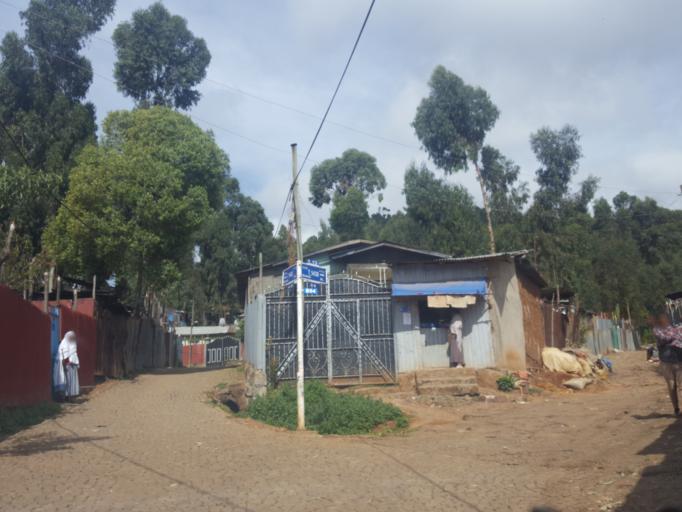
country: ET
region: Adis Abeba
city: Addis Ababa
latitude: 9.0668
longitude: 38.7470
